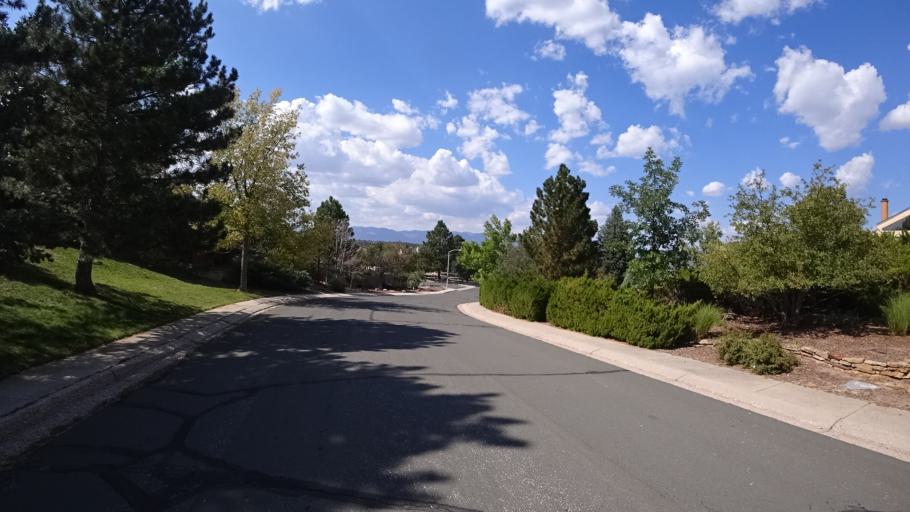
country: US
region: Colorado
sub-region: El Paso County
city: Cimarron Hills
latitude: 38.8702
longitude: -104.7444
